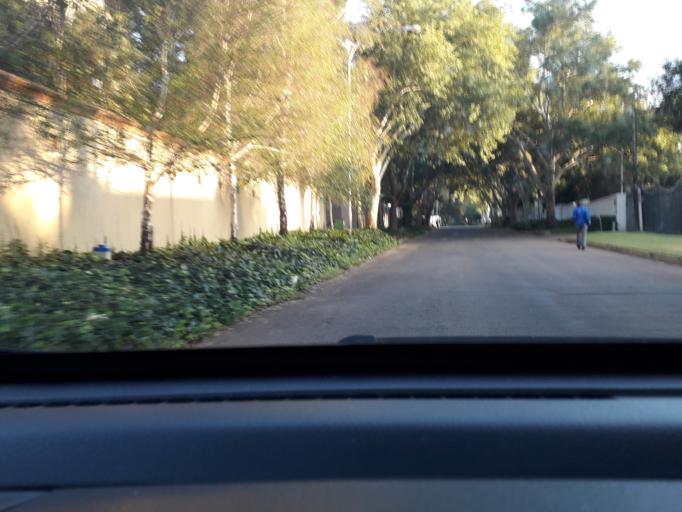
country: ZA
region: Gauteng
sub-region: City of Johannesburg Metropolitan Municipality
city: Johannesburg
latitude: -26.1548
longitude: 28.0516
